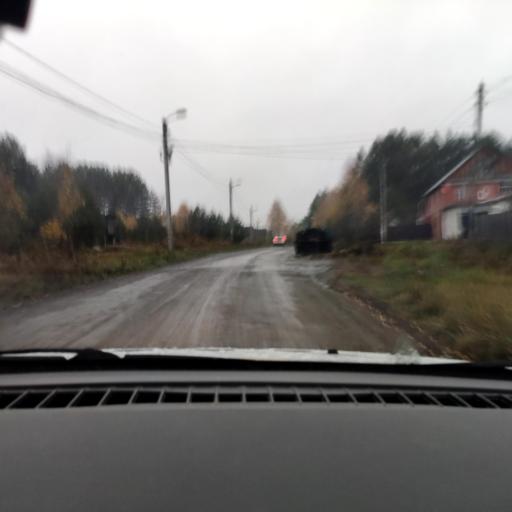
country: RU
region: Perm
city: Kondratovo
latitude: 58.0484
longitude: 56.1032
